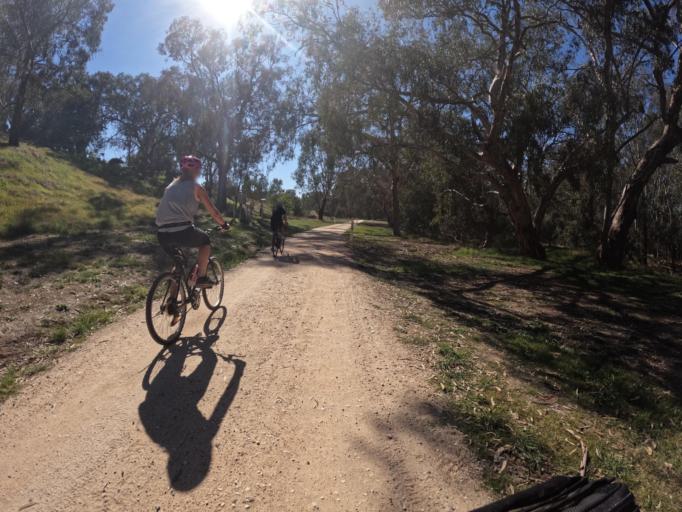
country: AU
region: Victoria
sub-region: Greater Bendigo
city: Epsom
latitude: -36.7930
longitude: 144.5052
